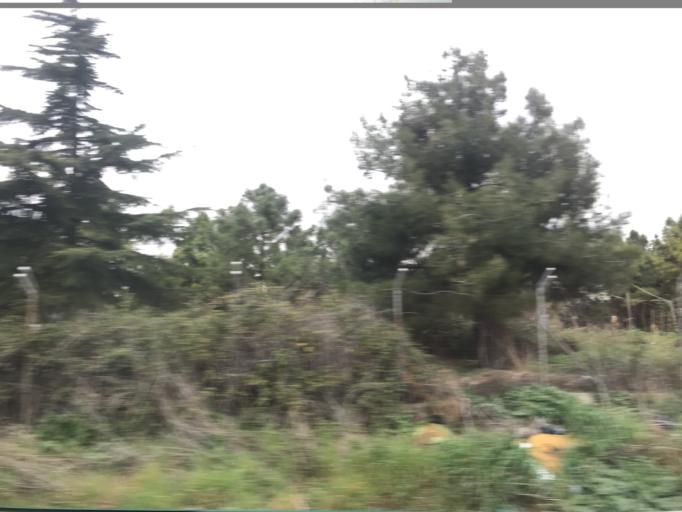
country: TR
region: Istanbul
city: Bahcelievler
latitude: 40.9643
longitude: 28.8058
